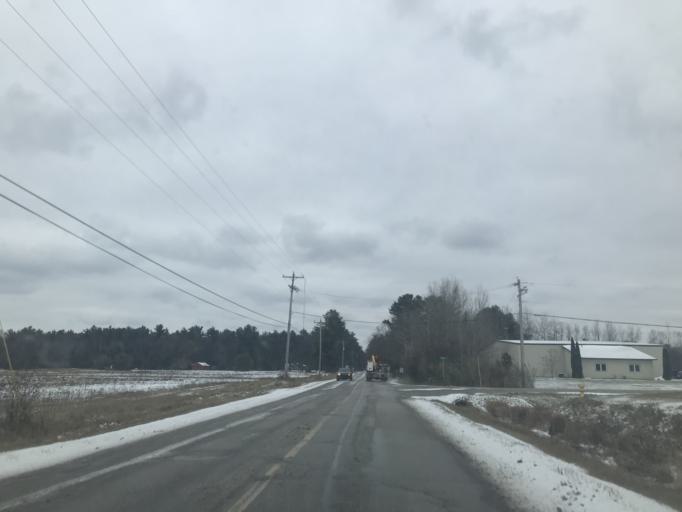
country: US
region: Wisconsin
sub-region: Marinette County
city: Marinette
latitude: 45.0710
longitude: -87.6596
